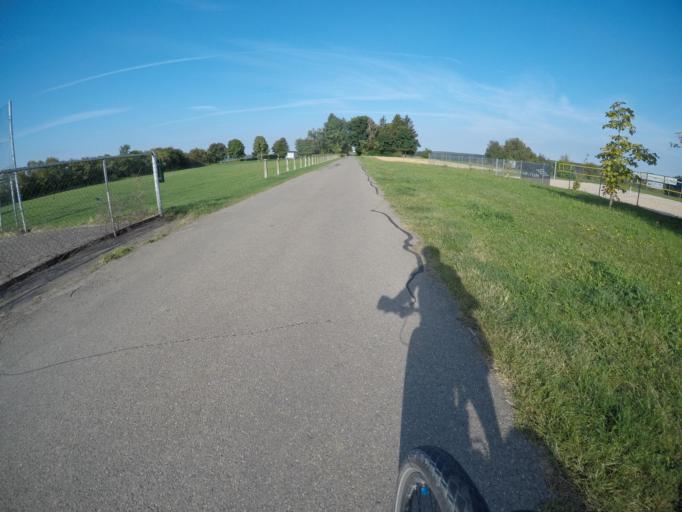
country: DE
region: Baden-Wuerttemberg
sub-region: Regierungsbezirk Stuttgart
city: Bolheim
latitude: 48.6008
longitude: 10.1178
